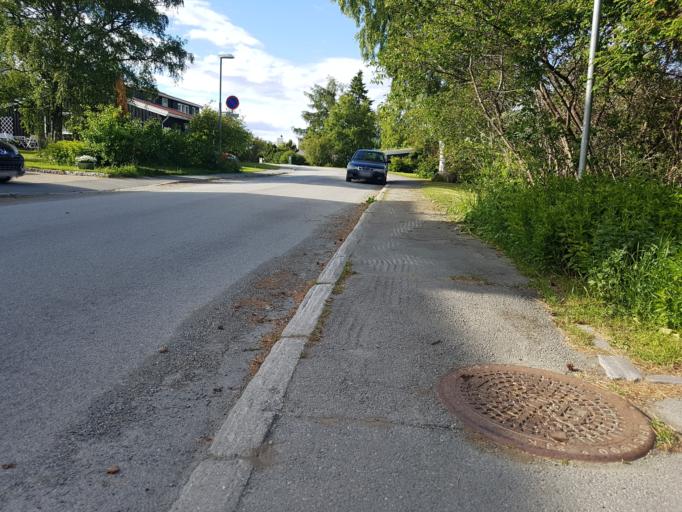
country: NO
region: Sor-Trondelag
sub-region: Trondheim
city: Trondheim
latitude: 63.4197
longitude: 10.3670
